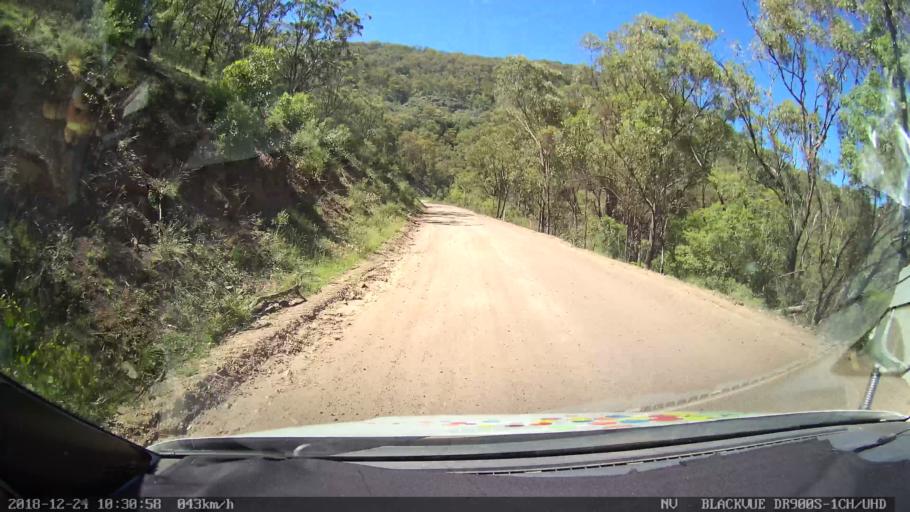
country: AU
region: New South Wales
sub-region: Upper Hunter Shire
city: Merriwa
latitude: -31.8373
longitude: 150.5232
